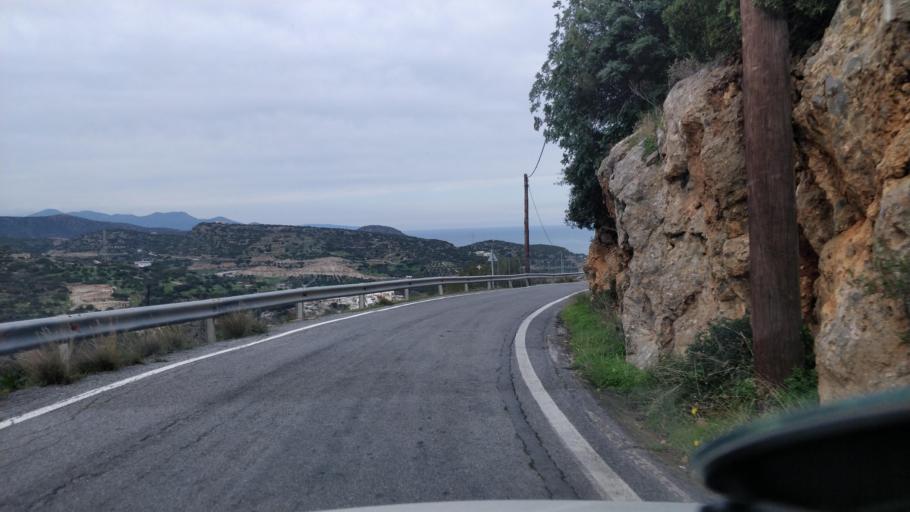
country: GR
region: Crete
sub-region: Nomos Lasithiou
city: Agios Nikolaos
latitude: 35.1095
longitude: 25.7163
